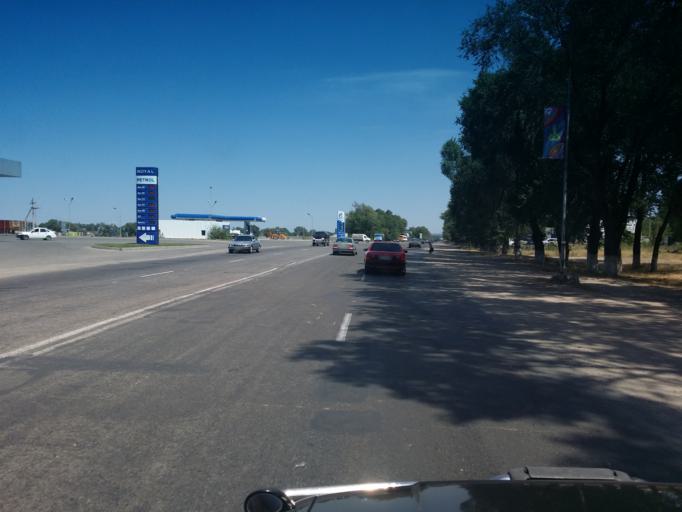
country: KZ
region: Almaty Oblysy
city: Talghar
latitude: 43.4079
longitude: 77.2434
